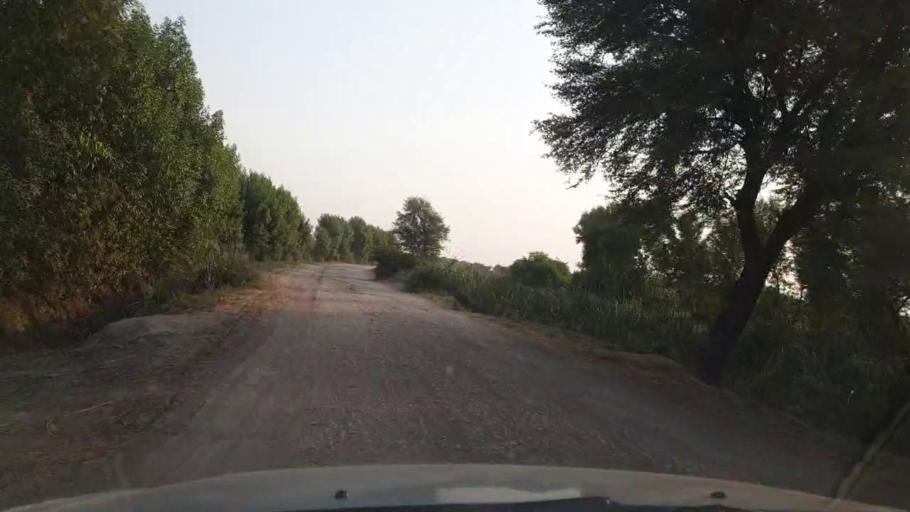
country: PK
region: Sindh
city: Tando Muhammad Khan
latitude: 25.0153
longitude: 68.4382
